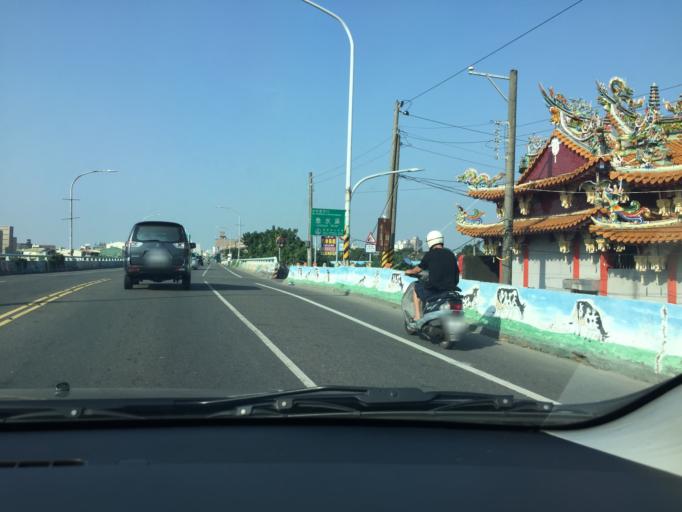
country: TW
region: Taiwan
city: Xinying
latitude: 23.2943
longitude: 120.3127
